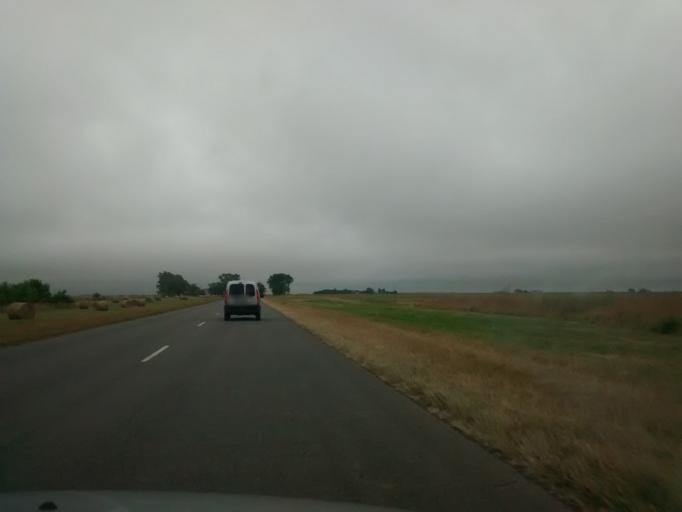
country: AR
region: Buenos Aires
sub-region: Partido de Ayacucho
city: Ayacucho
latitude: -37.2443
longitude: -58.4889
